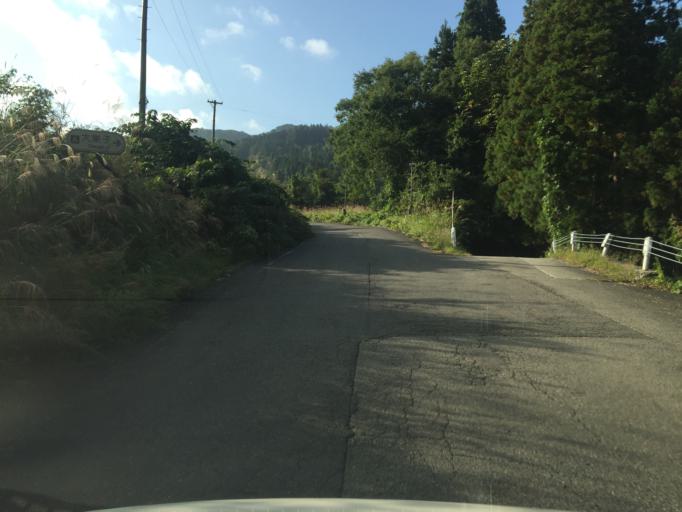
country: JP
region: Fukushima
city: Inawashiro
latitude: 37.4347
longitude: 139.9729
